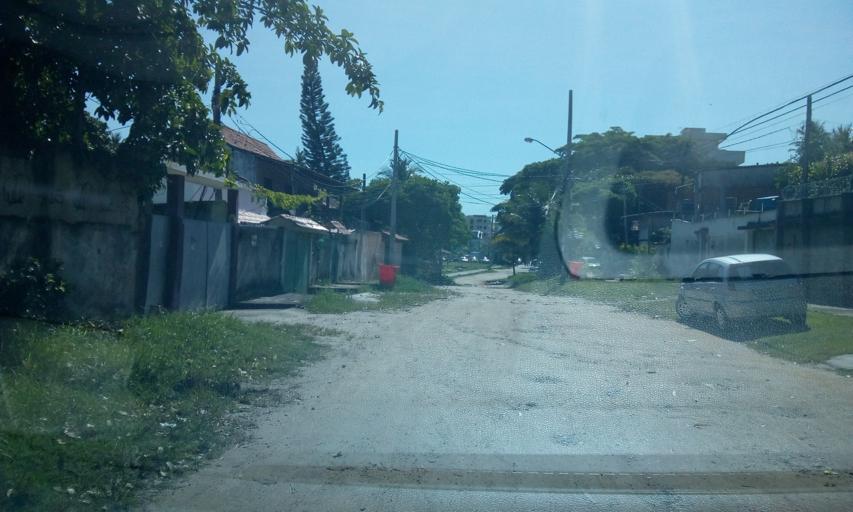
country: BR
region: Rio de Janeiro
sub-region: Nilopolis
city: Nilopolis
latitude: -23.0286
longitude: -43.4785
